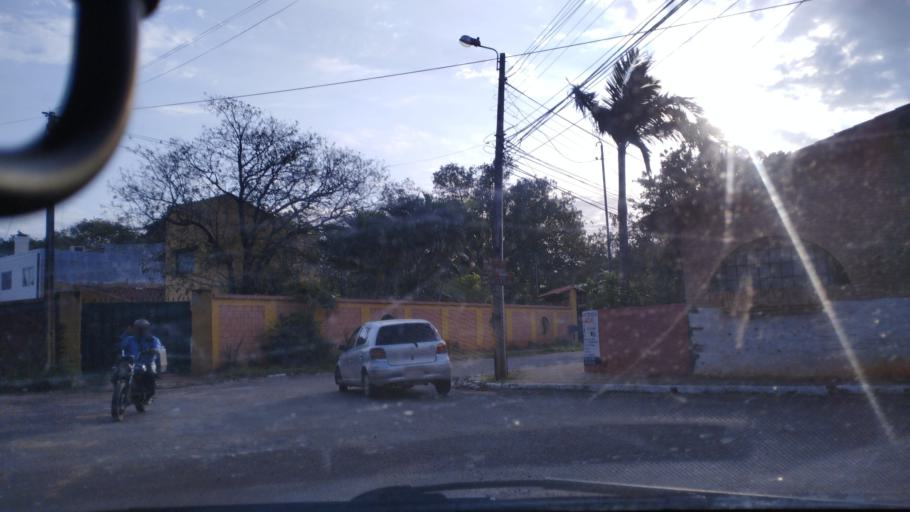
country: PY
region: Central
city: Fernando de la Mora
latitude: -25.3116
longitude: -57.5365
